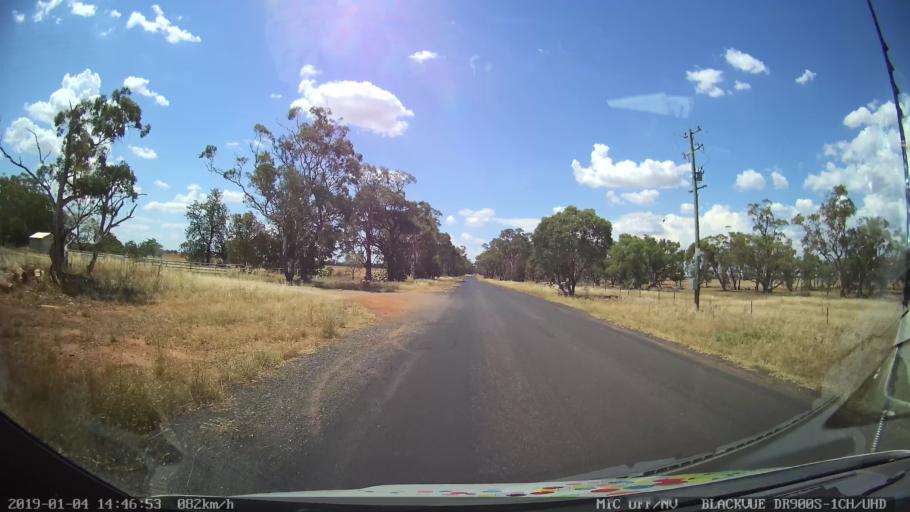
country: AU
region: New South Wales
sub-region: Dubbo Municipality
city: Dubbo
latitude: -32.0759
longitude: 148.6591
